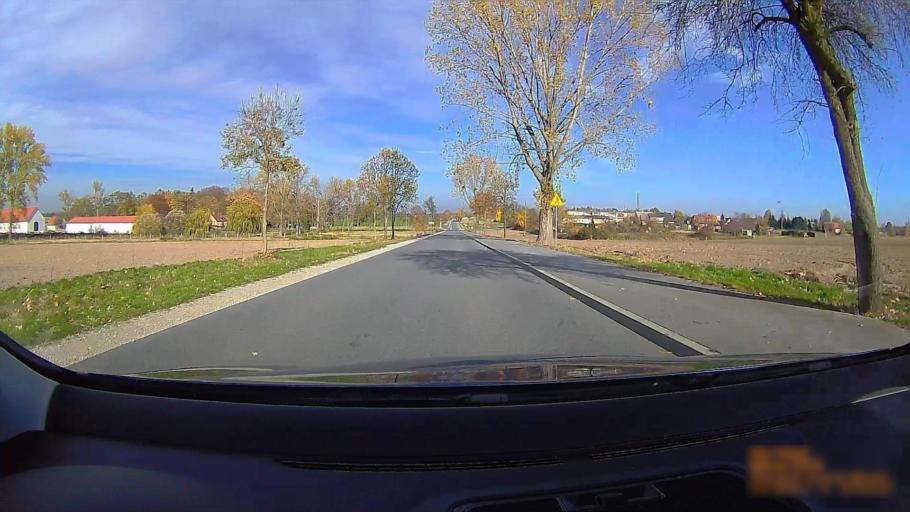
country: PL
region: Greater Poland Voivodeship
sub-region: Powiat kepinski
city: Kepno
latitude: 51.3427
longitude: 18.0231
